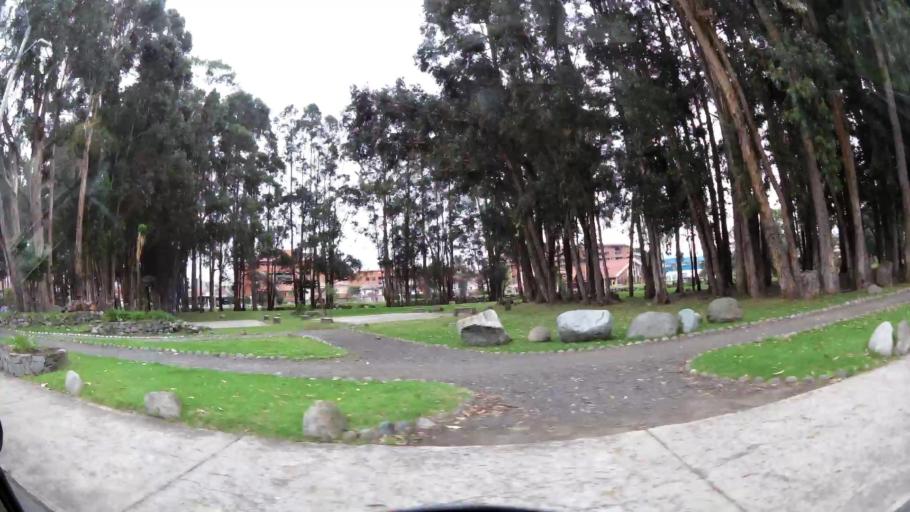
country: EC
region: Azuay
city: Cuenca
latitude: -2.9141
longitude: -79.0122
